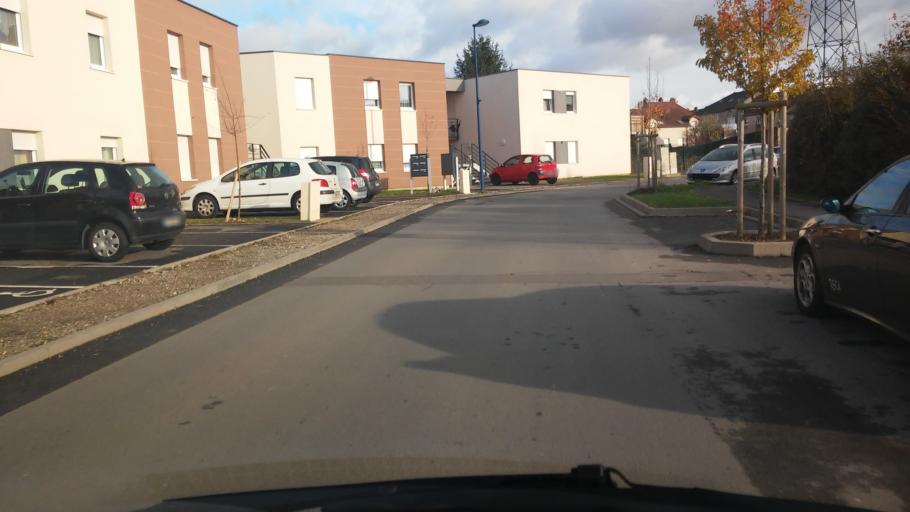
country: FR
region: Lorraine
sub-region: Departement de la Moselle
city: Talange
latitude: 49.2386
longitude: 6.1670
